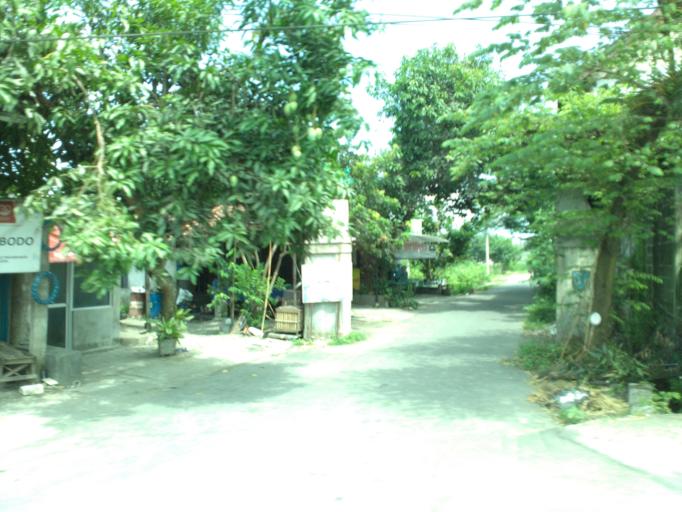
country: ID
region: Central Java
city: Candi Prambanan
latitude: -7.7510
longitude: 110.5193
